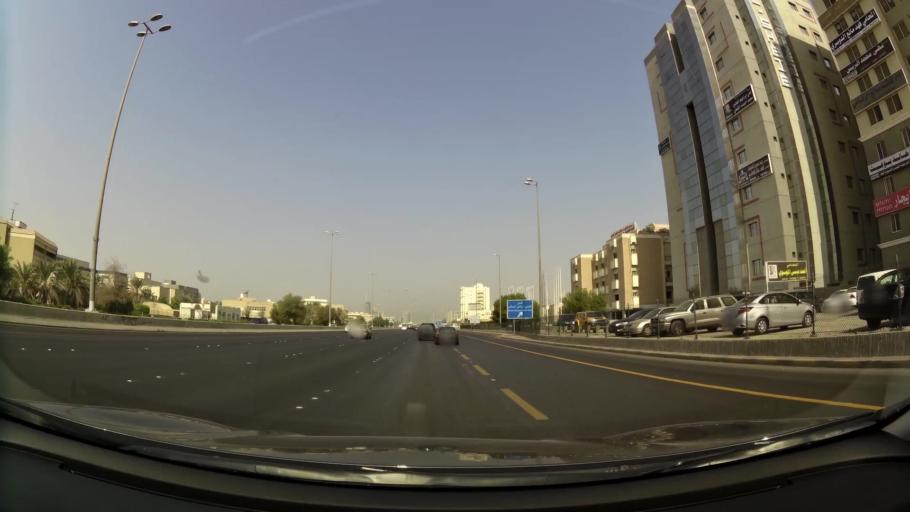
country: KW
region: Muhafazat Hawalli
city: Hawalli
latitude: 29.3345
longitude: 48.0046
